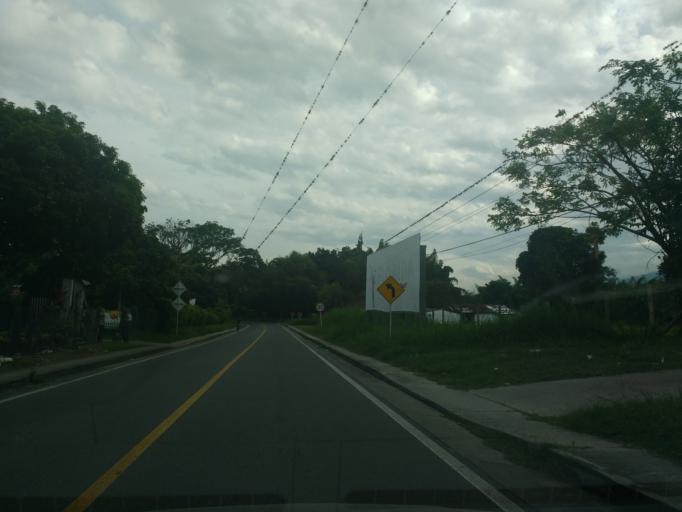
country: CO
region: Cauca
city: Miranda
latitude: 3.2778
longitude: -76.2215
